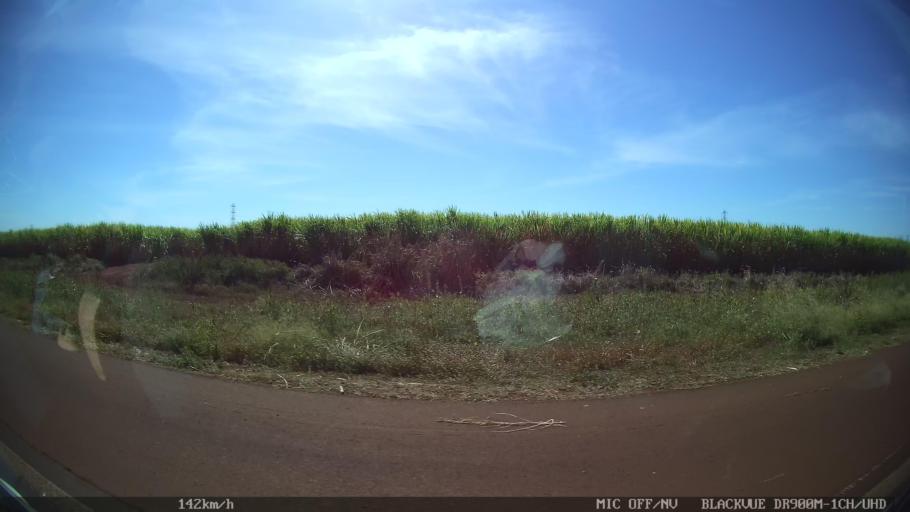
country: BR
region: Sao Paulo
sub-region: Guaira
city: Guaira
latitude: -20.4447
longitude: -48.2589
